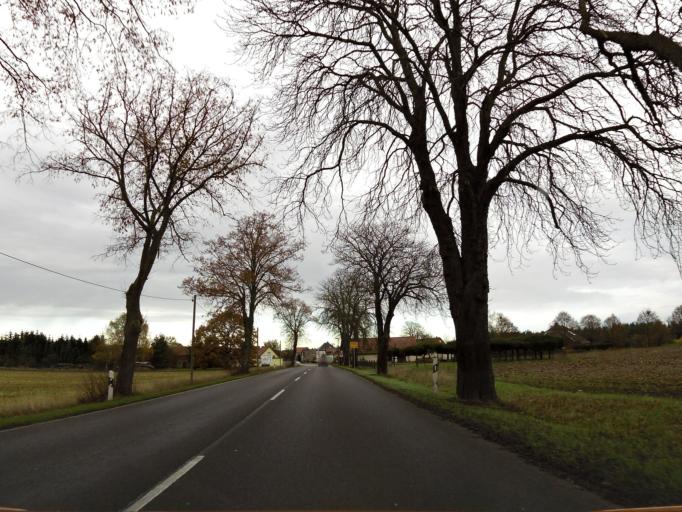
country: DE
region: Saxony-Anhalt
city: Letzlingen
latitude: 52.4378
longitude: 11.4828
